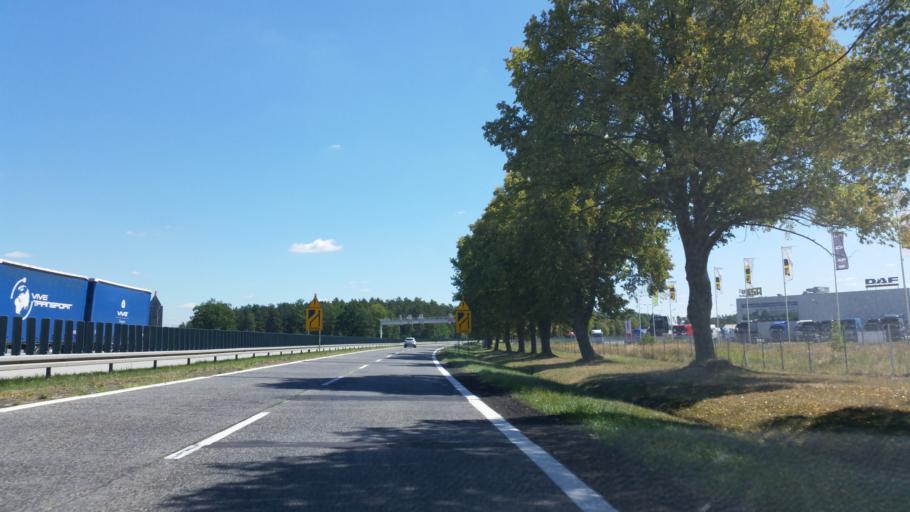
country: PL
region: Lubusz
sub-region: Powiat zaganski
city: Ilowa
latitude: 51.5286
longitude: 15.2027
